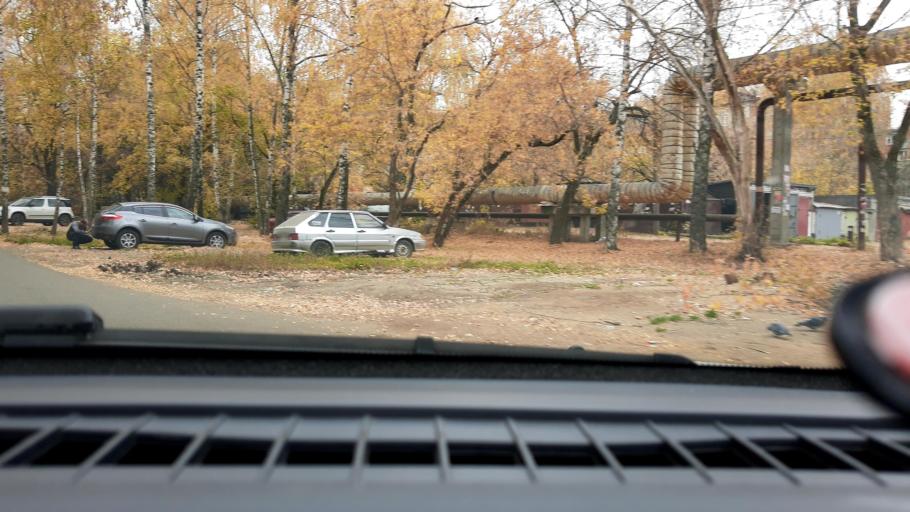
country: RU
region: Nizjnij Novgorod
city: Nizhniy Novgorod
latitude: 56.2737
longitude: 43.9145
